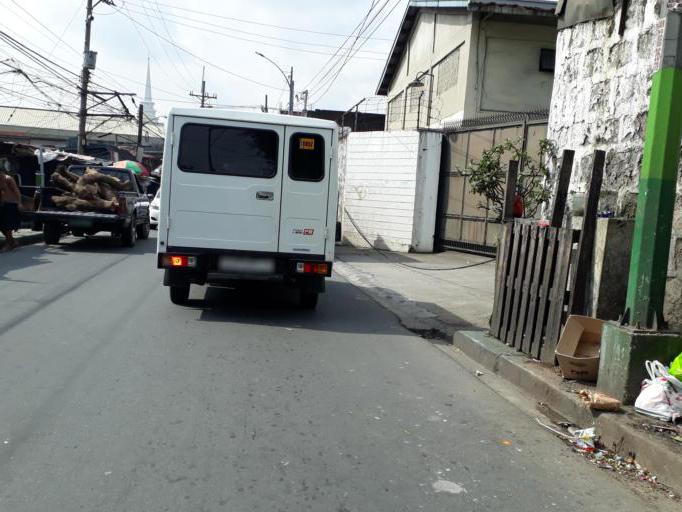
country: PH
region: Calabarzon
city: Bagong Pagasa
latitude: 14.6689
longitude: 121.0066
